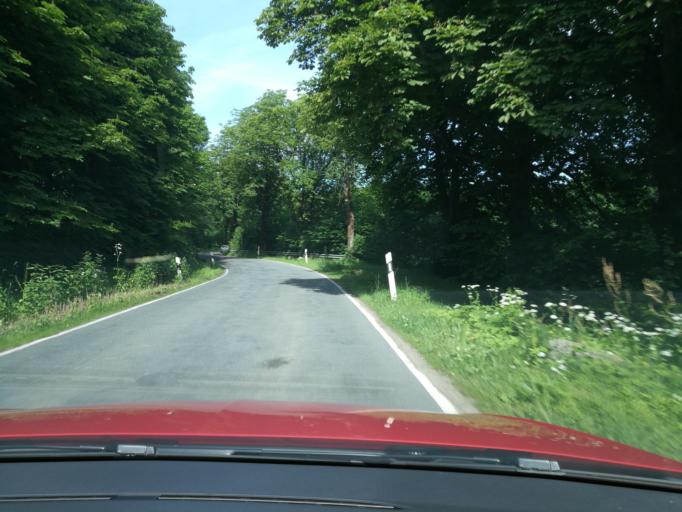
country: DE
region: Schleswig-Holstein
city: Tremsbuttel
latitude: 53.7443
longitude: 10.3385
